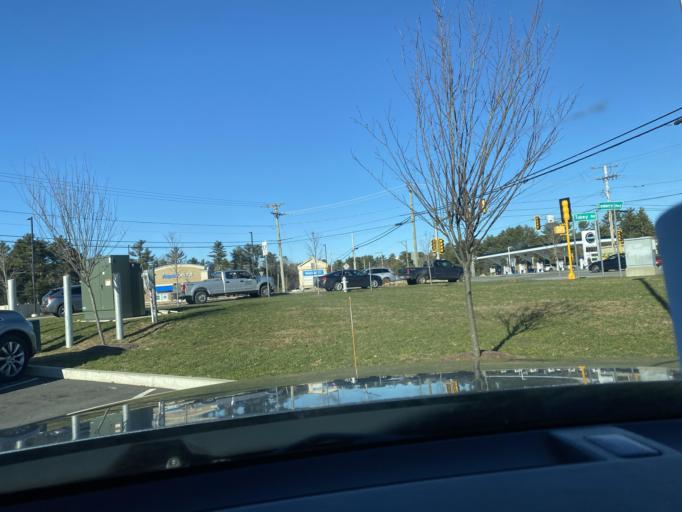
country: US
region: Massachusetts
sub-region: Plymouth County
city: West Wareham
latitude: 41.7807
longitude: -70.7440
